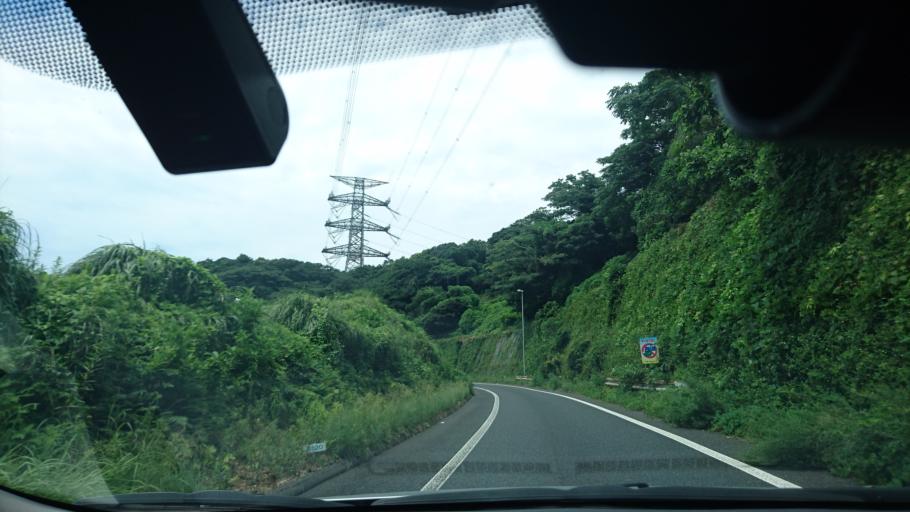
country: JP
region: Yamaguchi
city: Shimonoseki
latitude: 33.9653
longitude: 130.9541
